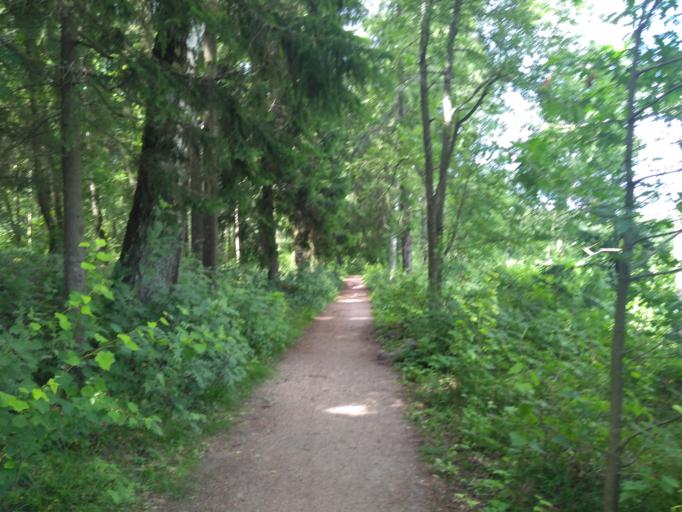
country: FI
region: Uusimaa
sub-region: Helsinki
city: Vantaa
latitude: 60.2173
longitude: 25.0112
